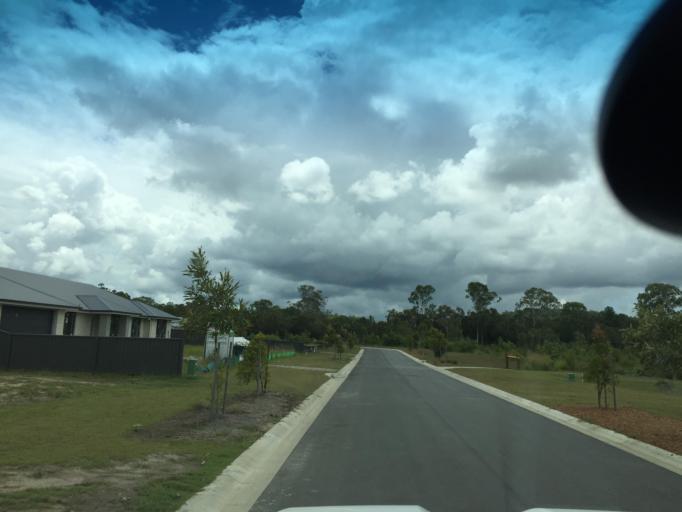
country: AU
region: Queensland
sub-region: Moreton Bay
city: Caboolture
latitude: -27.0412
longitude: 152.9263
